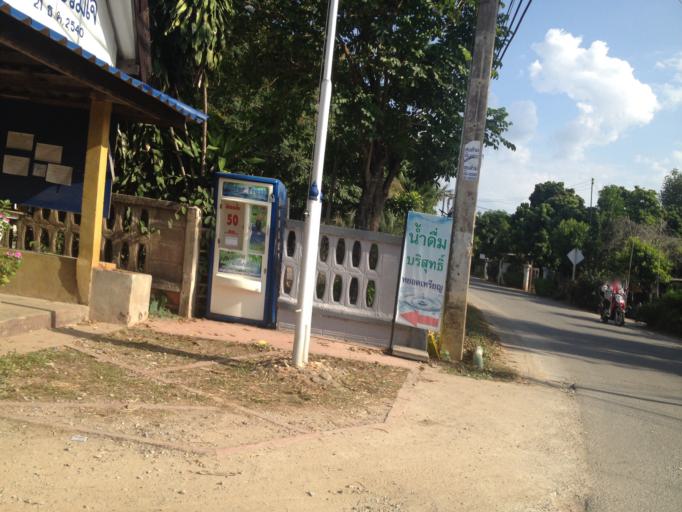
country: TH
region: Chiang Mai
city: Hang Dong
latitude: 18.7066
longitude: 98.9225
